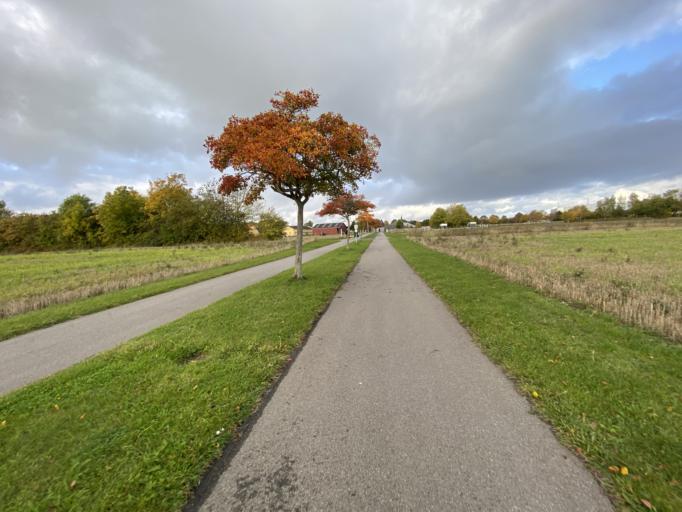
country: DK
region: Capital Region
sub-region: Dragor Kommune
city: Dragor
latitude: 55.5915
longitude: 12.6367
